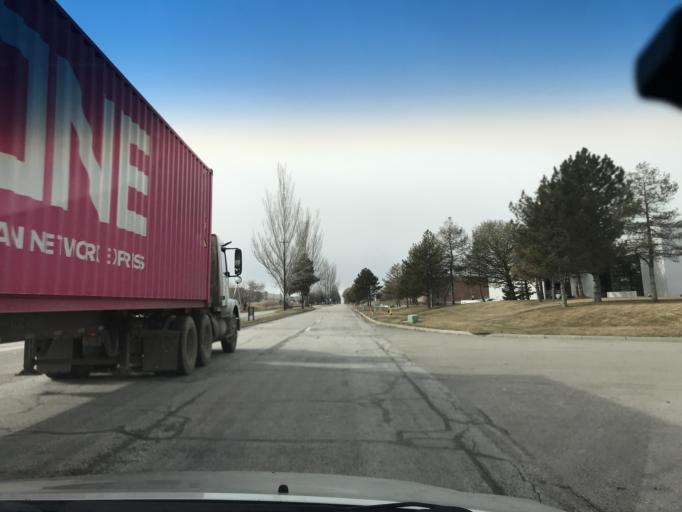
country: US
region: Utah
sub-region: Salt Lake County
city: West Valley City
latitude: 40.7814
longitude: -112.0104
